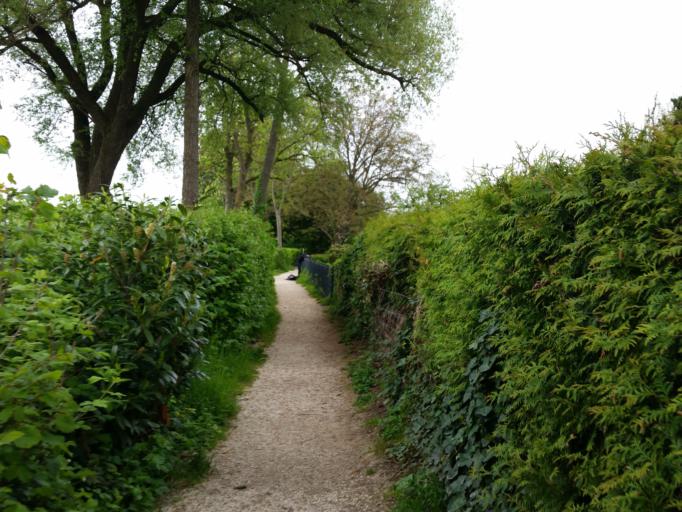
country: CH
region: Thurgau
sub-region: Arbon District
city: Uttwil
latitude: 47.5883
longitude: 9.3375
